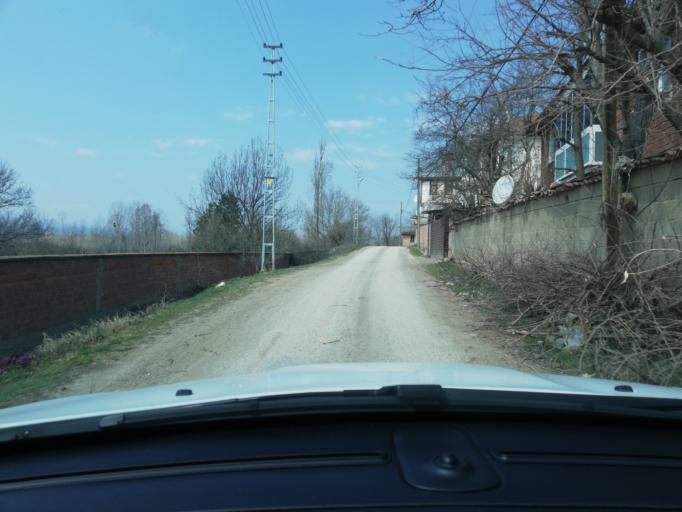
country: TR
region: Kastamonu
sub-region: Cide
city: Kastamonu
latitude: 41.4589
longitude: 33.7589
